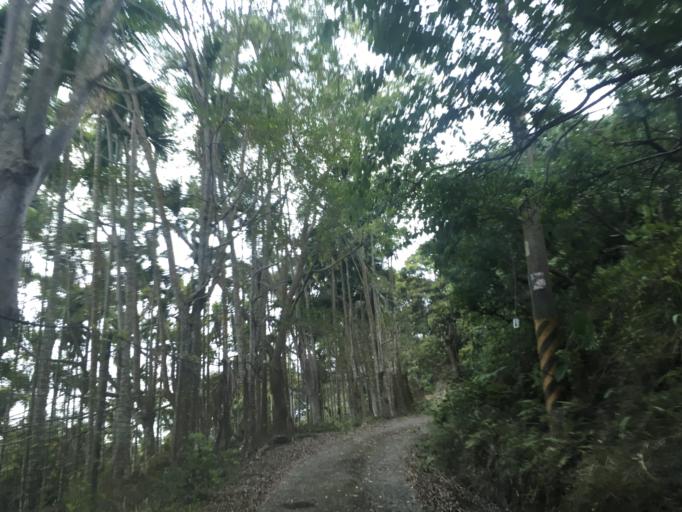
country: TW
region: Taiwan
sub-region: Taichung City
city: Taichung
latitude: 24.1359
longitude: 120.8209
